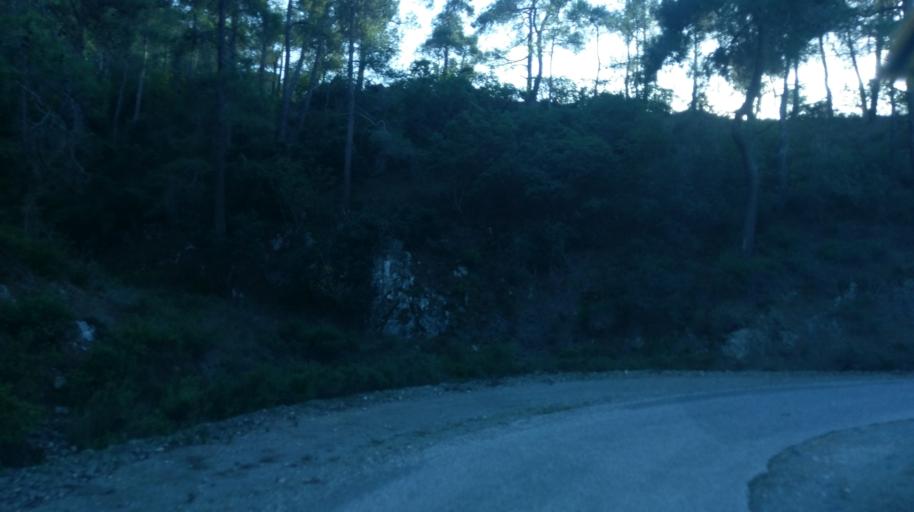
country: CY
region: Ammochostos
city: Lefkonoiko
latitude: 35.3064
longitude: 33.5720
